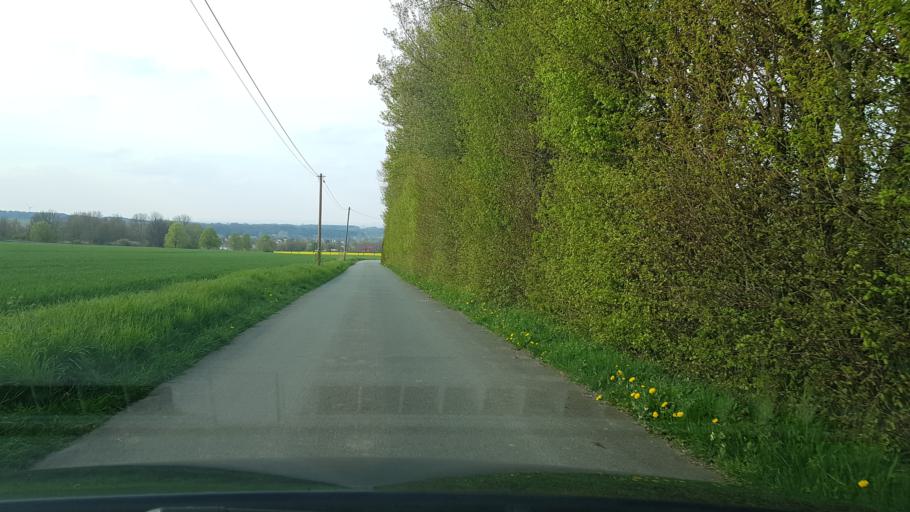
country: DE
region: North Rhine-Westphalia
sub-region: Regierungsbezirk Detmold
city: Paderborn
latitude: 51.6458
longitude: 8.7204
